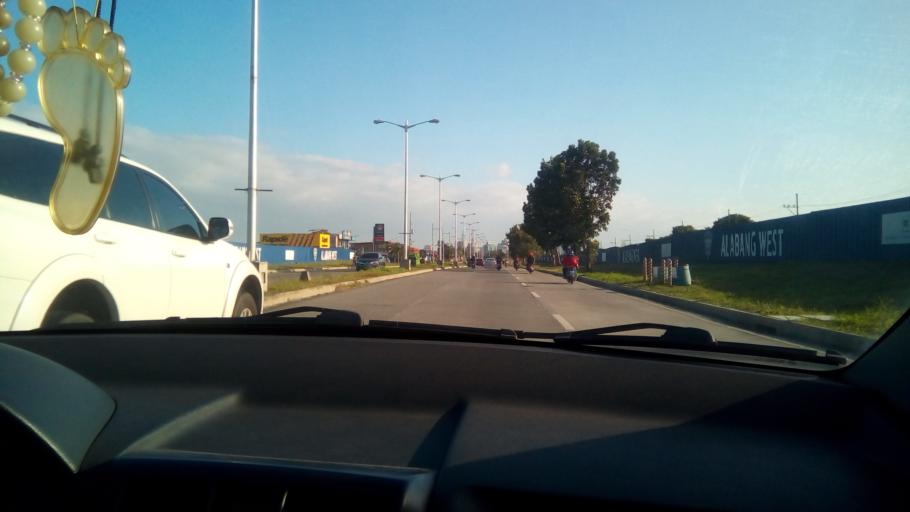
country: PH
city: Sambayanihan People's Village
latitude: 14.4107
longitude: 121.0144
